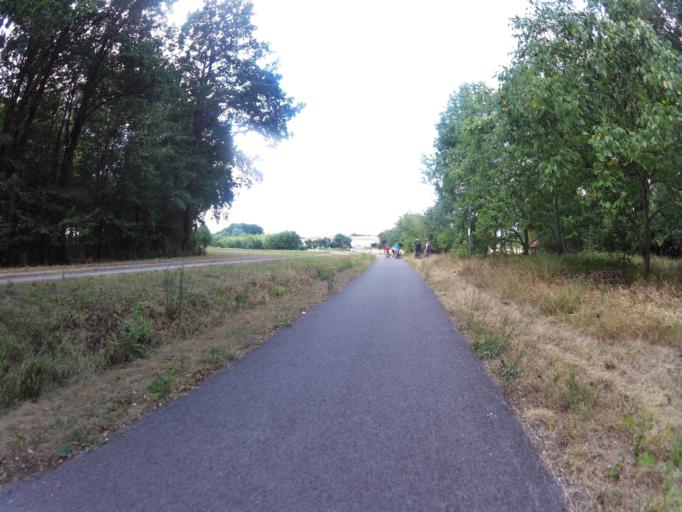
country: DE
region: Bavaria
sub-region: Regierungsbezirk Unterfranken
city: Bieberehren
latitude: 49.5319
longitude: 10.0340
